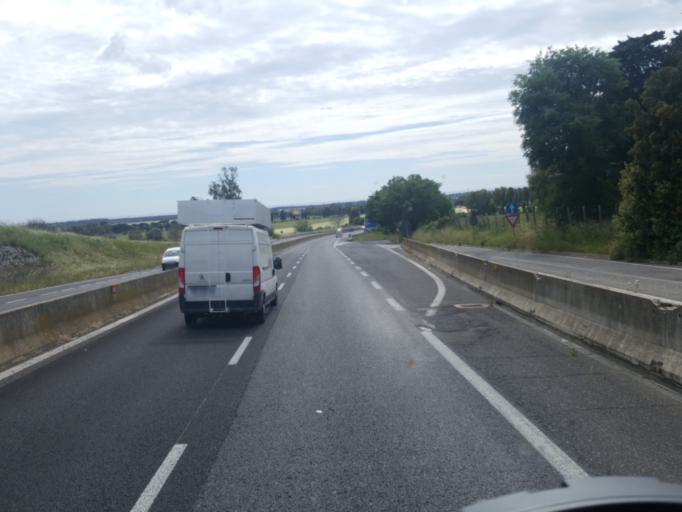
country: IT
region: Latium
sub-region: Citta metropolitana di Roma Capitale
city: Ara Nova
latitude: 41.9160
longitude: 12.2268
